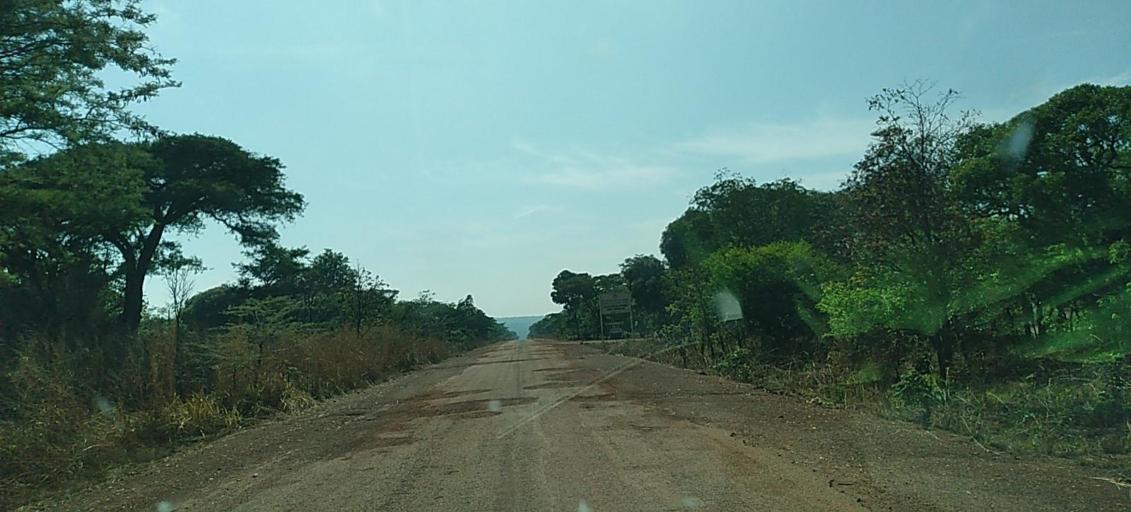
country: ZM
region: North-Western
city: Mwinilunga
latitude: -11.8218
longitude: 25.1022
